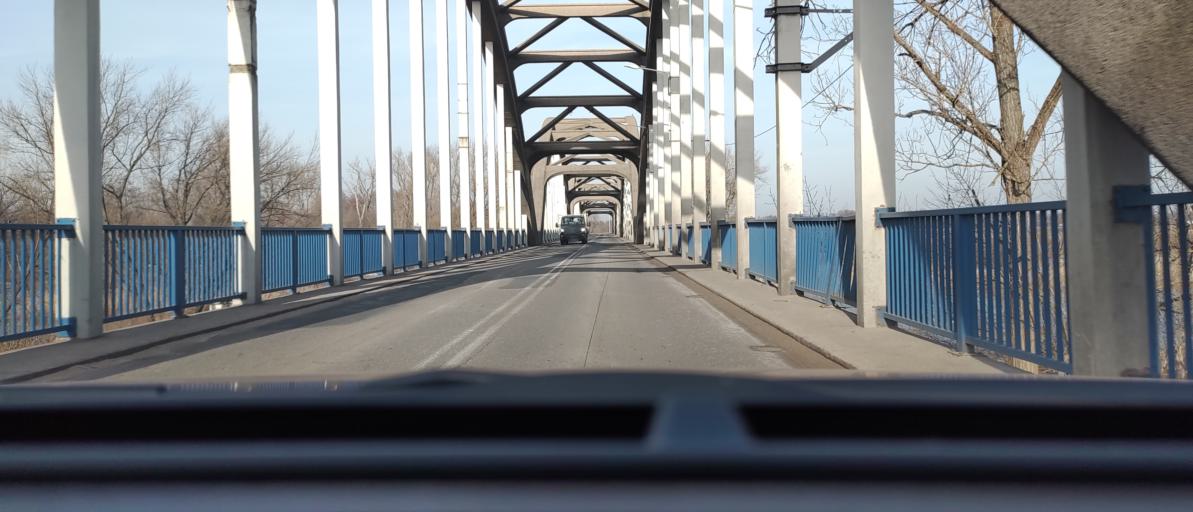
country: PL
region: Masovian Voivodeship
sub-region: Powiat bialobrzeski
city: Bialobrzegi
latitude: 51.6571
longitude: 20.9511
